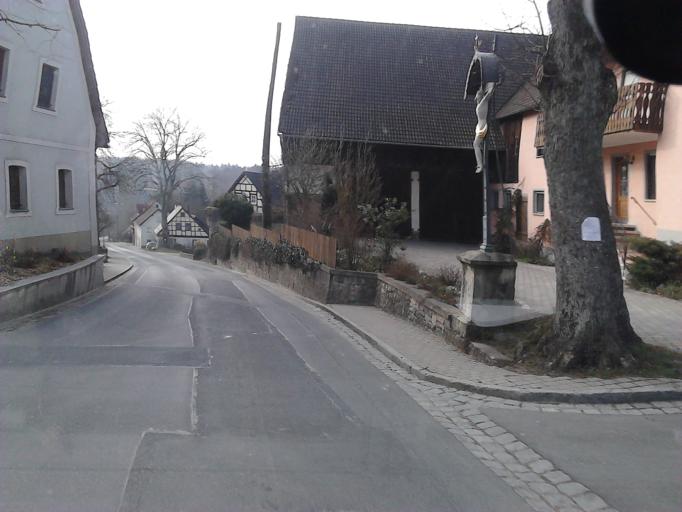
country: DE
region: Bavaria
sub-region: Upper Franconia
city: Wattendorf
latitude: 50.0325
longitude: 11.1250
